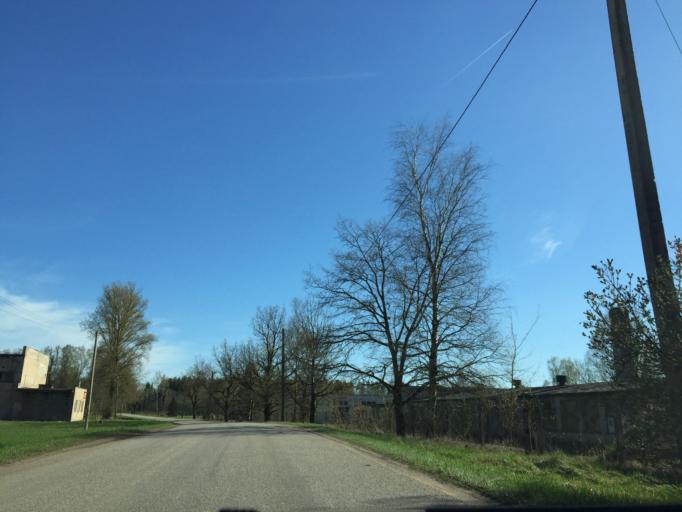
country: EE
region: Valgamaa
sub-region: Valga linn
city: Valga
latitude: 57.8678
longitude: 26.2510
